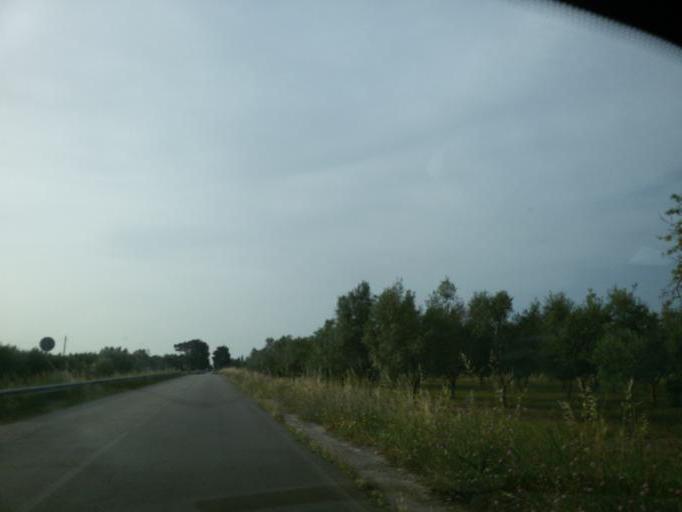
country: IT
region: Apulia
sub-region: Provincia di Brindisi
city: San Pietro Vernotico
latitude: 40.5134
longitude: 17.9888
